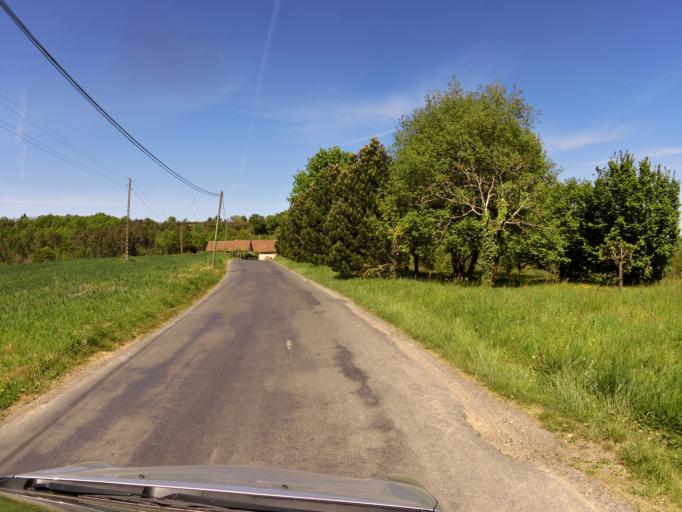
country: FR
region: Aquitaine
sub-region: Departement de la Dordogne
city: Sarlat-la-Caneda
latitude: 44.9185
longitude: 1.1966
